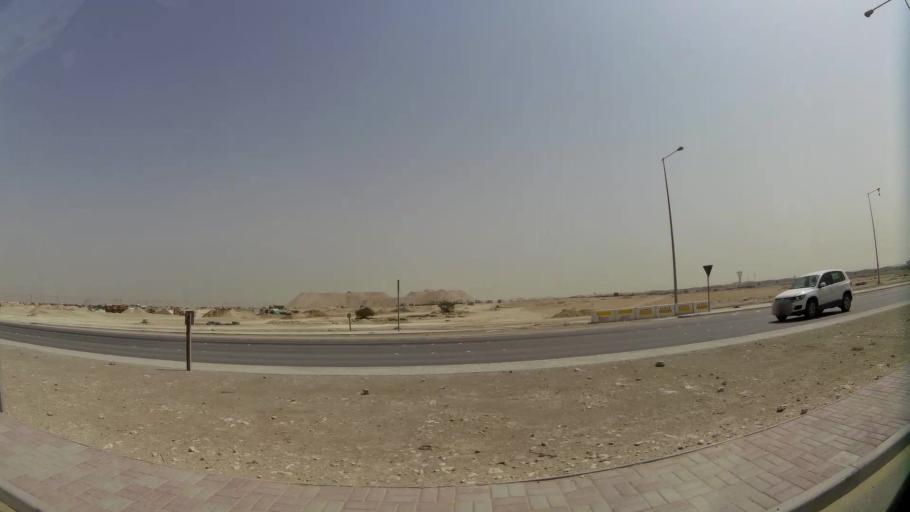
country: QA
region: Baladiyat ar Rayyan
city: Ar Rayyan
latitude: 25.1727
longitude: 51.4000
